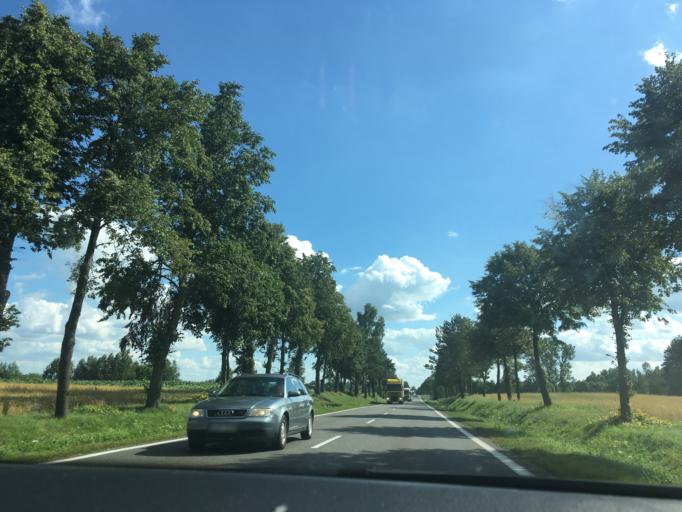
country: PL
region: Podlasie
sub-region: Powiat sokolski
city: Janow
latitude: 53.4049
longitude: 23.1169
